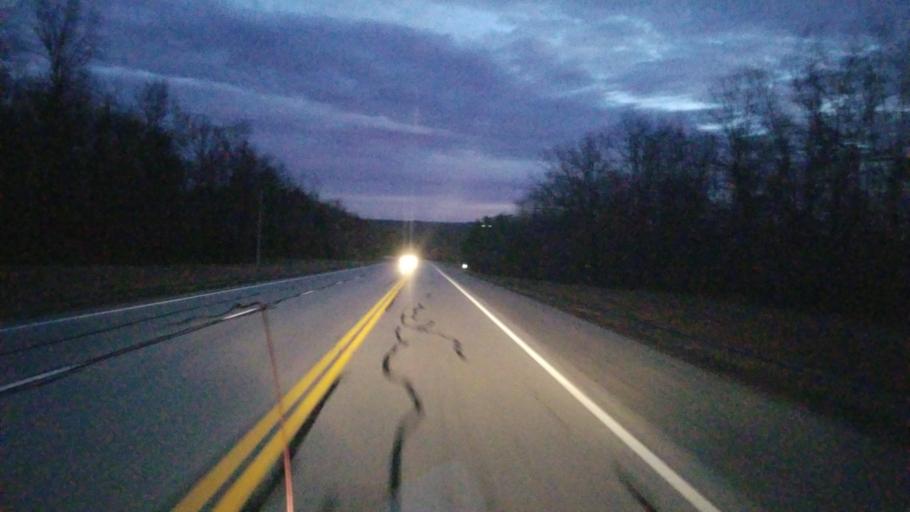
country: US
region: Tennessee
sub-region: Sequatchie County
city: Dunlap
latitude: 35.5153
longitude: -85.4718
